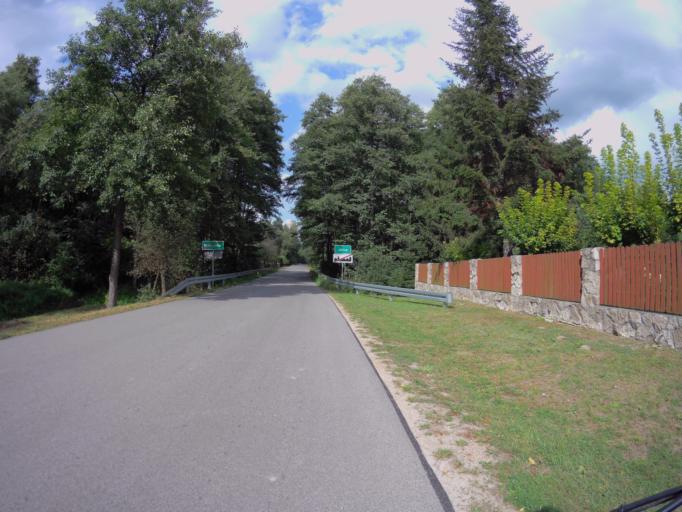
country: PL
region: Subcarpathian Voivodeship
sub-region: Powiat lezajski
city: Brzoza Krolewska
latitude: 50.2742
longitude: 22.3527
